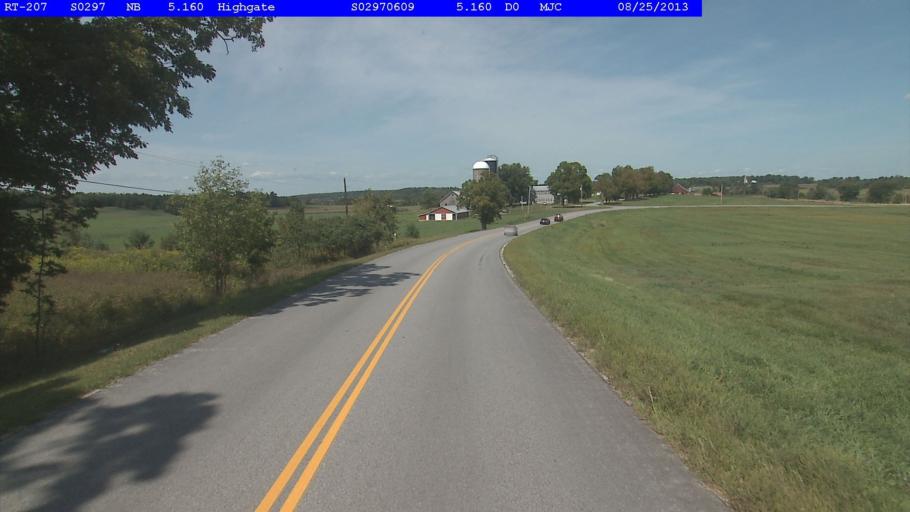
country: CA
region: Quebec
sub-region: Monteregie
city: Bedford
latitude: 45.0028
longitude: -73.0008
